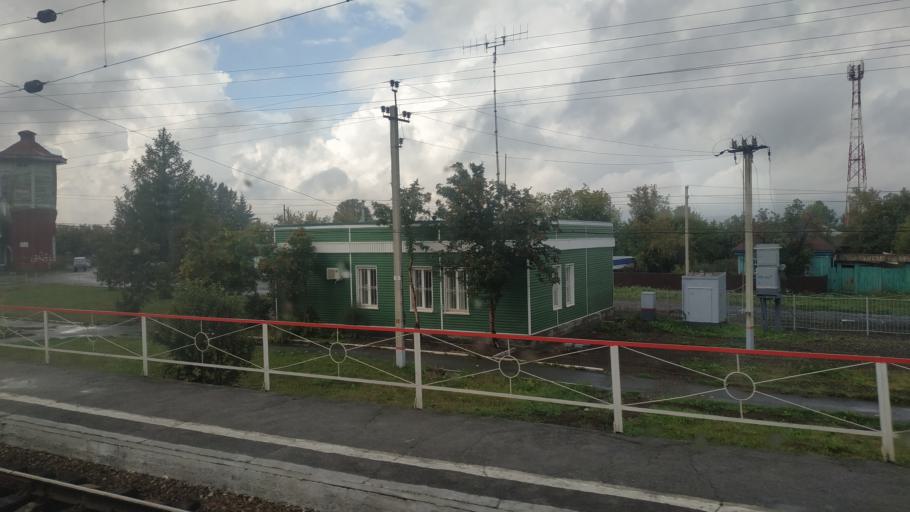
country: RU
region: Novosibirsk
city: Stantsionno-Oyashinskiy
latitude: 55.4628
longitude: 83.8214
